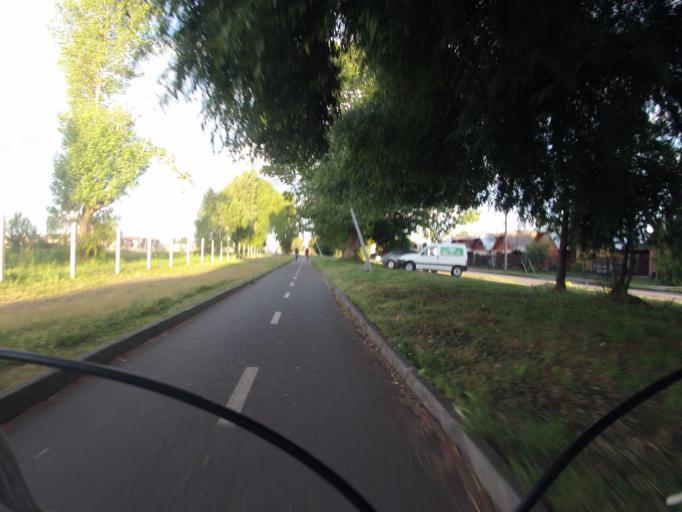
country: CL
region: Araucania
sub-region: Provincia de Cautin
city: Temuco
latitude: -38.7522
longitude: -72.6496
